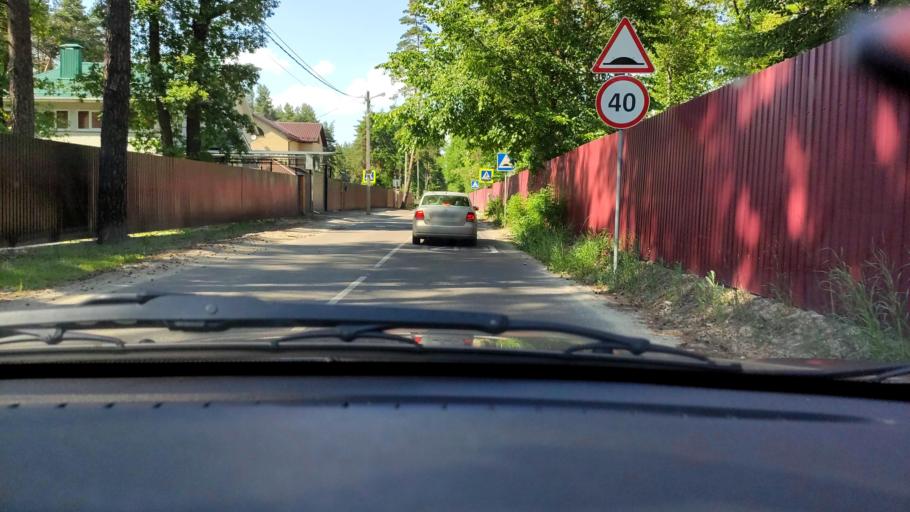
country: RU
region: Voronezj
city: Somovo
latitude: 51.7549
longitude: 39.3661
